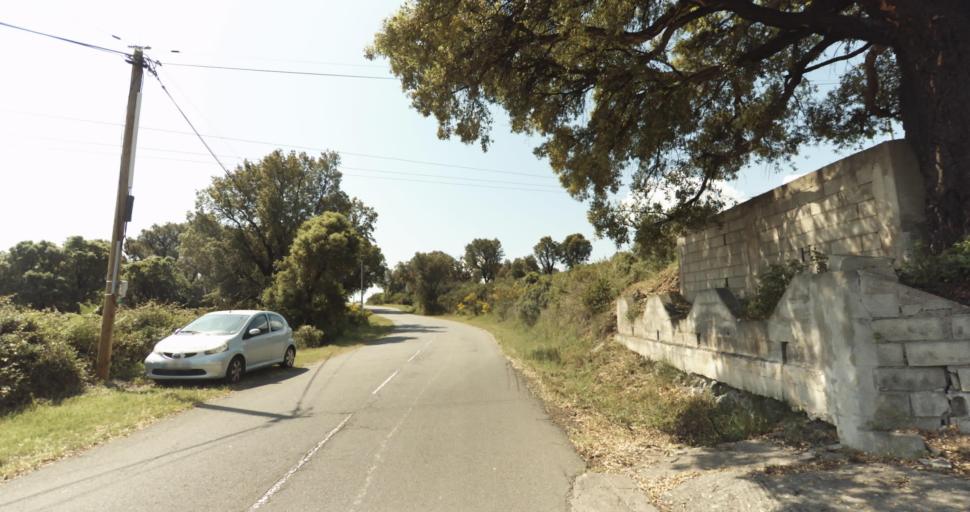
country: FR
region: Corsica
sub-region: Departement de la Haute-Corse
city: Biguglia
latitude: 42.6174
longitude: 9.4232
